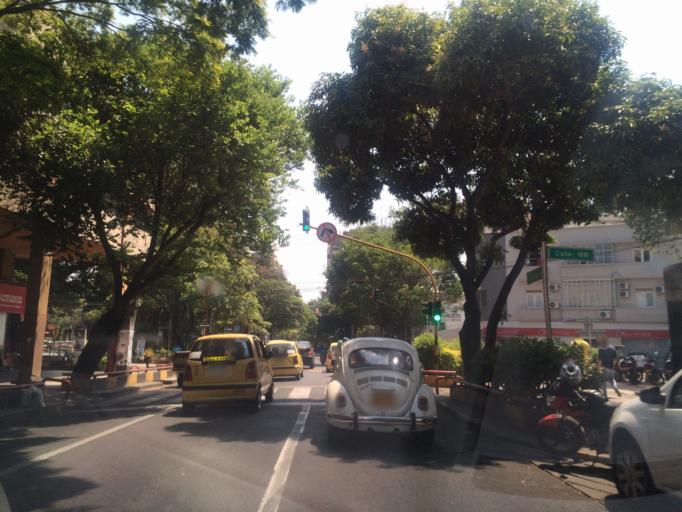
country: CO
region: Valle del Cauca
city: Cali
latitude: 3.4609
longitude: -76.5312
